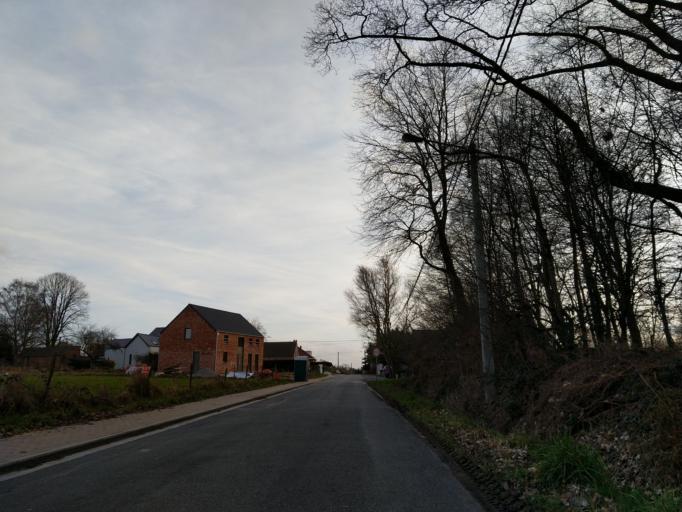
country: BE
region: Wallonia
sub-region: Province du Hainaut
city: Jurbise
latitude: 50.5150
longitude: 3.9503
